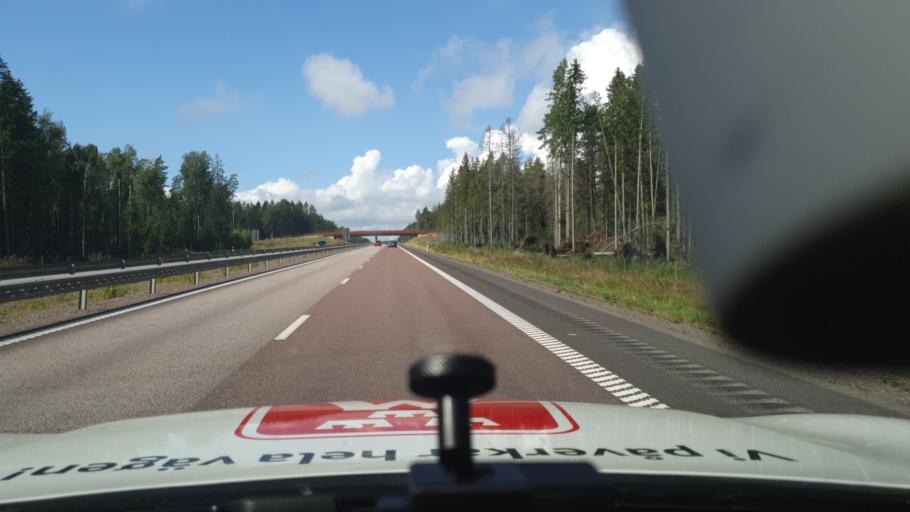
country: SE
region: Vaermland
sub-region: Hammaro Kommun
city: Skoghall
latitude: 59.3818
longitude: 13.3781
